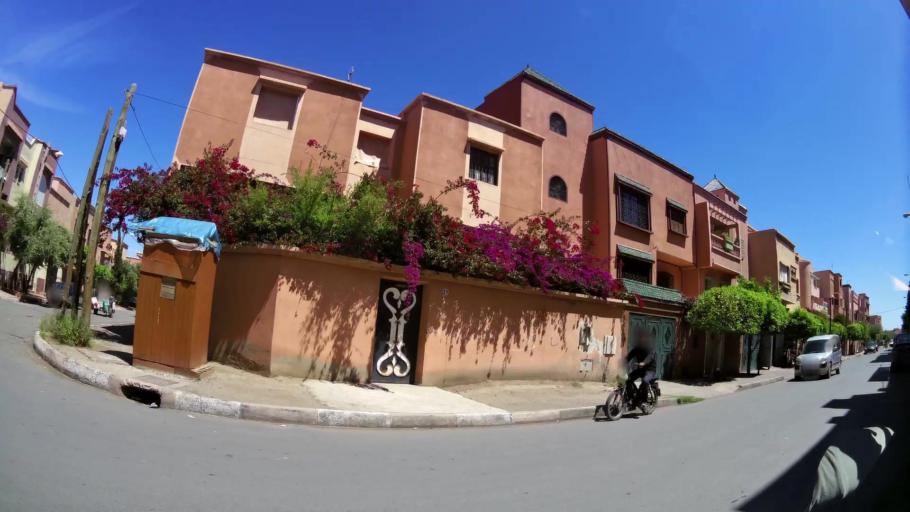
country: MA
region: Marrakech-Tensift-Al Haouz
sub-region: Marrakech
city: Marrakesh
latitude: 31.6374
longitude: -8.0616
